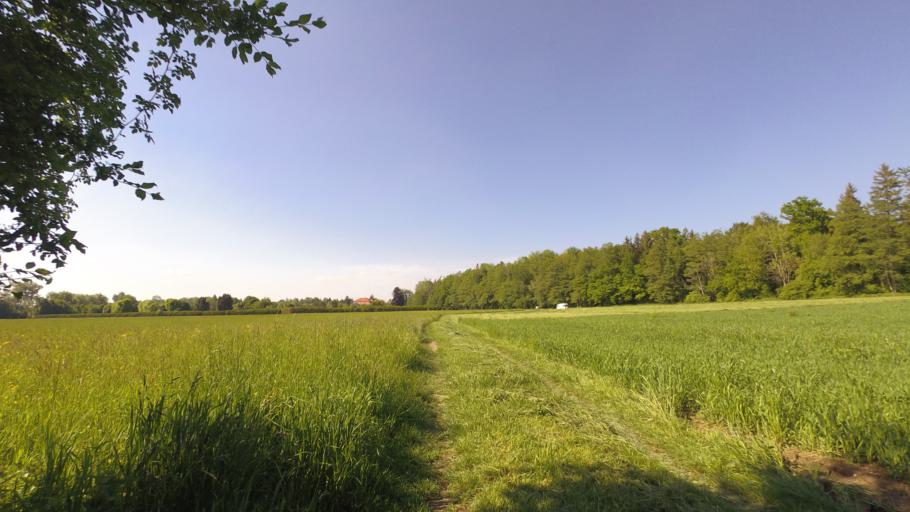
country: DE
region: Bavaria
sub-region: Upper Bavaria
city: Seeon-Seebruck
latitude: 47.9265
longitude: 12.4962
